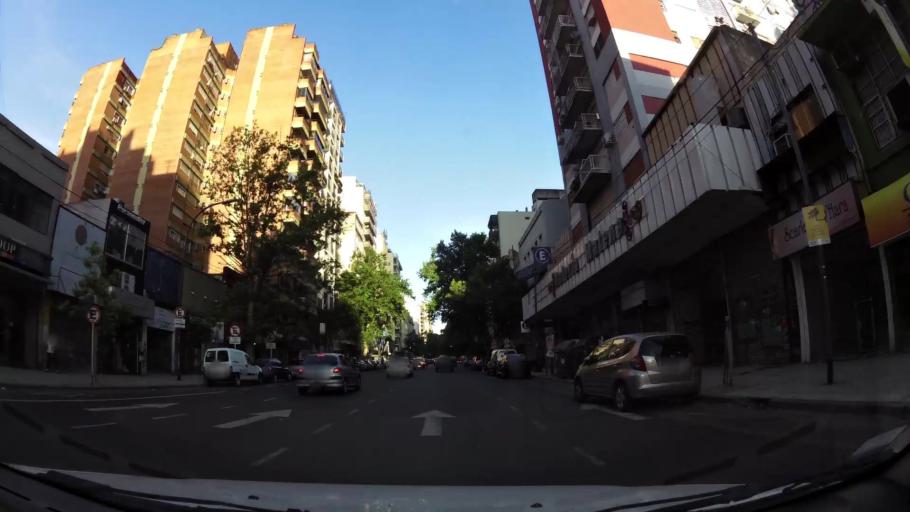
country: AR
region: Buenos Aires F.D.
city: Buenos Aires
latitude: -34.6046
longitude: -58.3980
